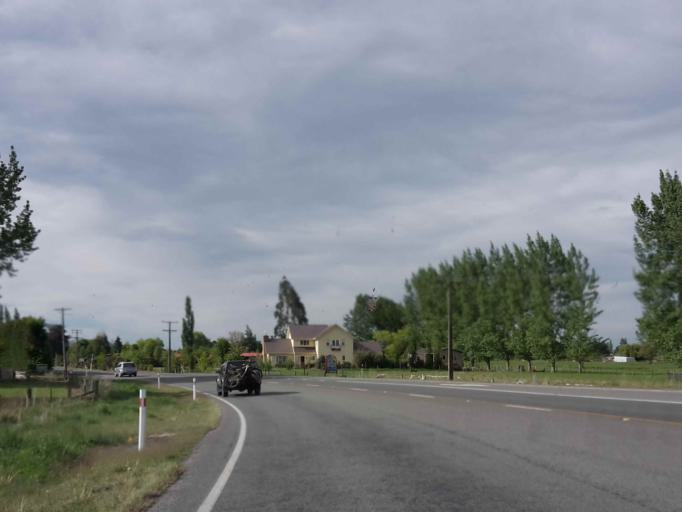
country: NZ
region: Canterbury
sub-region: Timaru District
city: Pleasant Point
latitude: -44.1068
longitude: 171.2368
